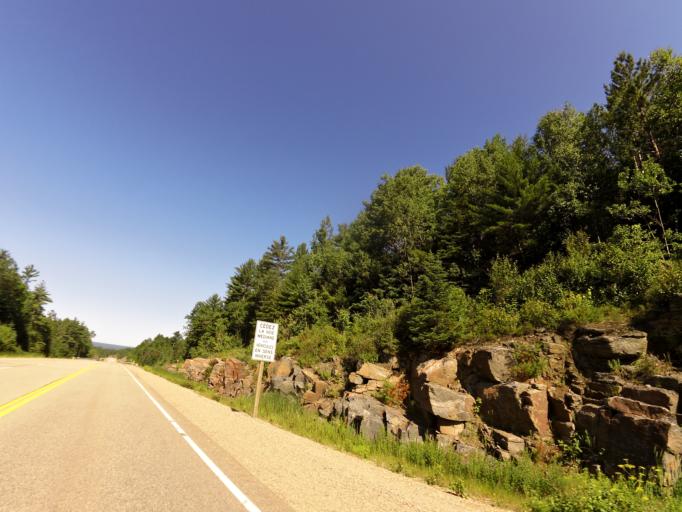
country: CA
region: Ontario
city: Mattawa
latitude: 46.2582
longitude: -78.2296
